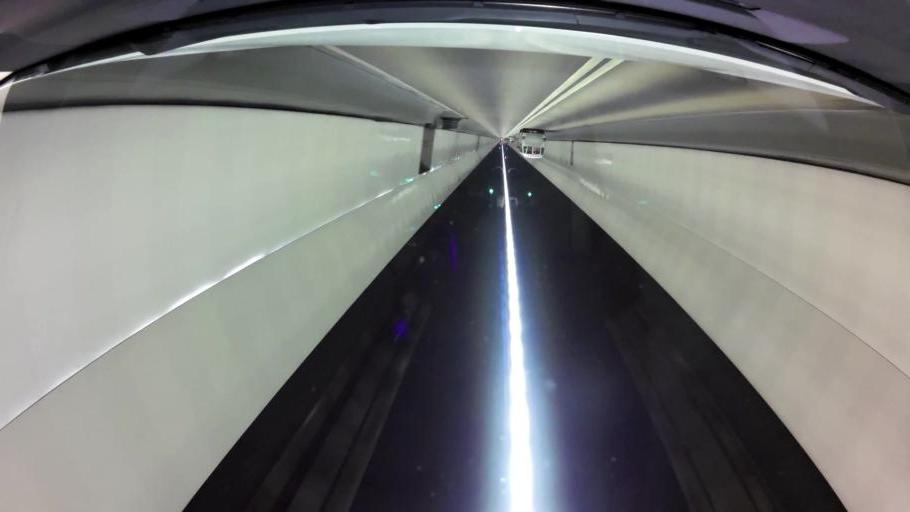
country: HK
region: Sha Tin
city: Sha Tin
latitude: 22.3772
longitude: 114.1538
